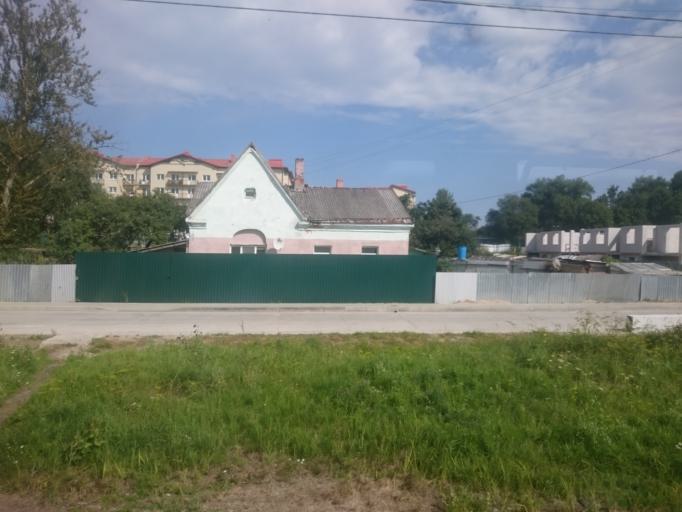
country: RU
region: Kaliningrad
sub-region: Zelenogradskiy Rayon
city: Zelenogradsk
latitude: 54.9507
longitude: 20.4572
